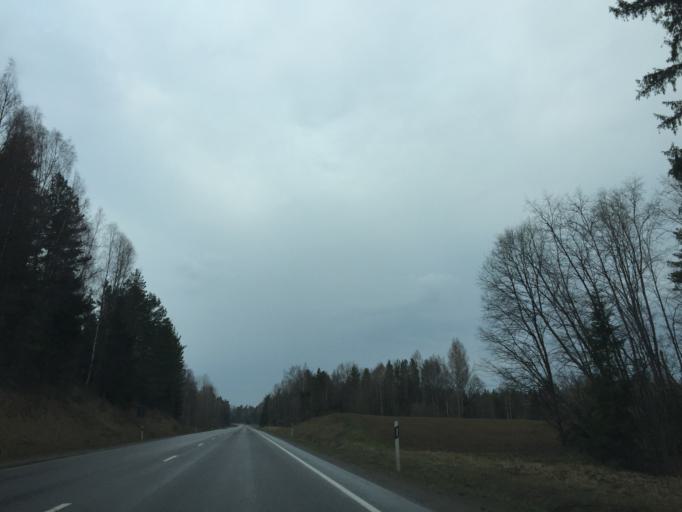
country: EE
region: Tartu
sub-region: UElenurme vald
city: Ulenurme
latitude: 58.1169
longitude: 26.7342
